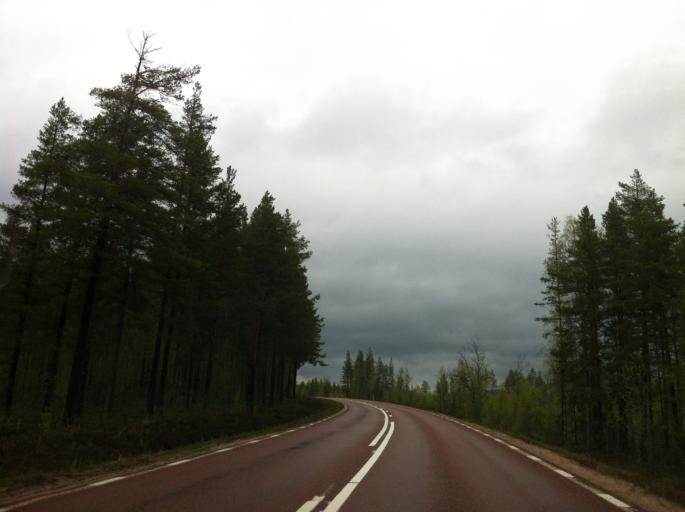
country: SE
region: Jaemtland
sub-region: Harjedalens Kommun
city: Sveg
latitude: 61.8954
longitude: 14.6237
